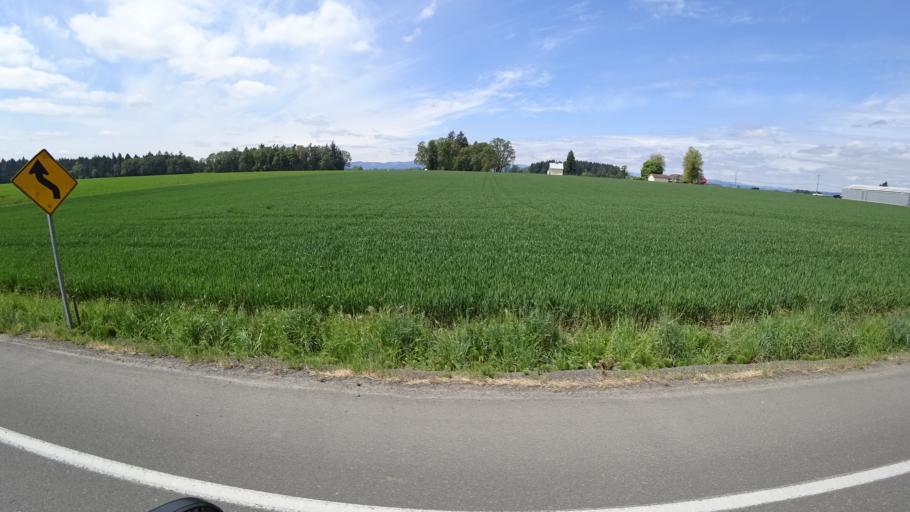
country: US
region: Oregon
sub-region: Washington County
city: North Plains
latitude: 45.5608
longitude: -122.9994
